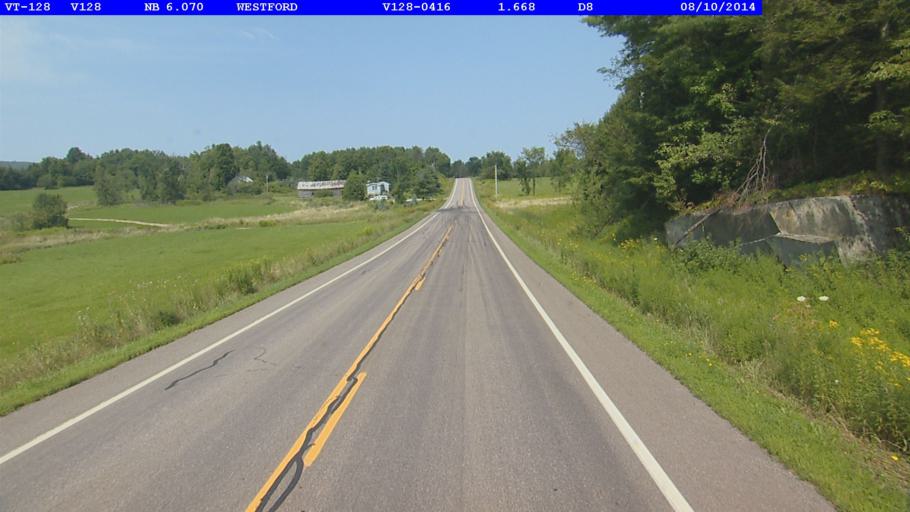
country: US
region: Vermont
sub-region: Chittenden County
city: Jericho
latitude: 44.5819
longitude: -73.0174
